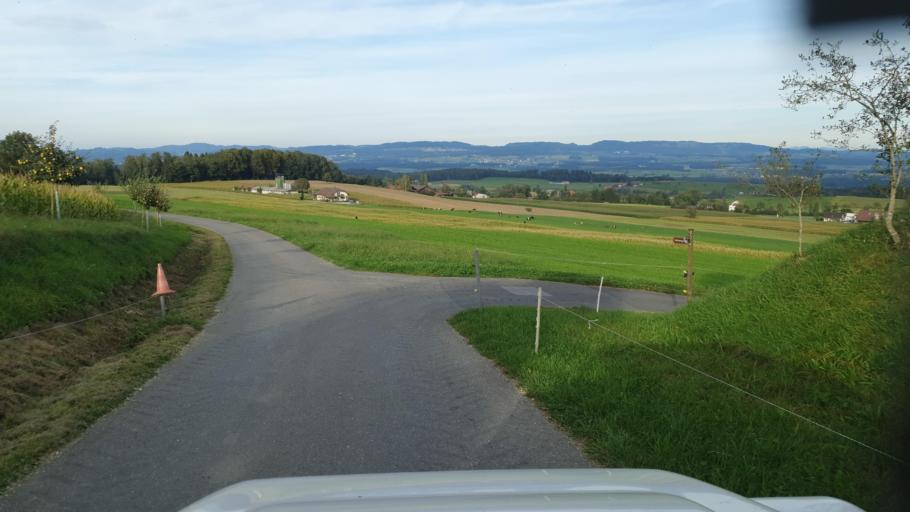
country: CH
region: Aargau
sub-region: Bezirk Muri
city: Auw
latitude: 47.1900
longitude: 8.3490
